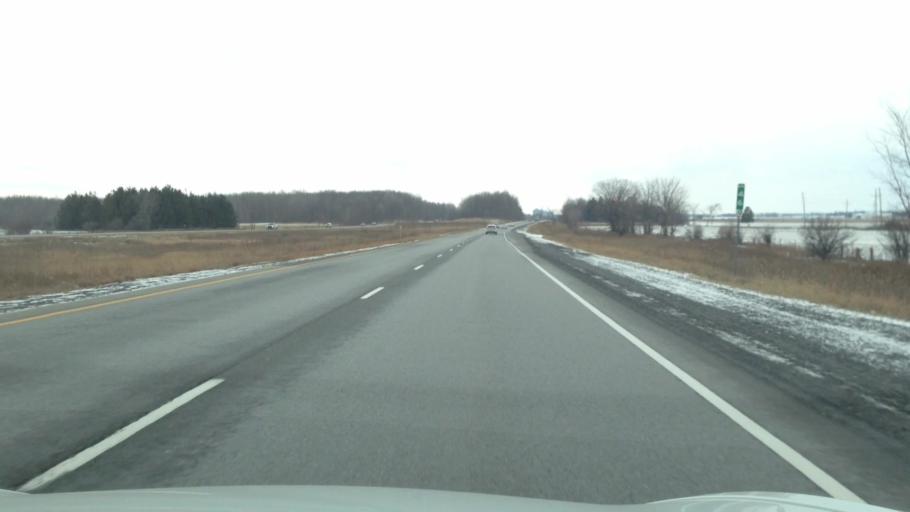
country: CA
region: Ontario
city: Casselman
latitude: 45.3711
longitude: -74.8532
